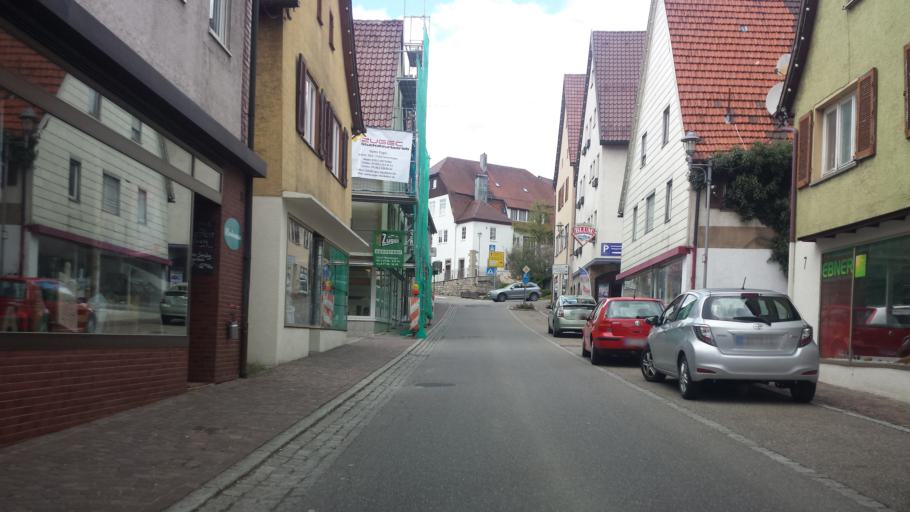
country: DE
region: Baden-Wuerttemberg
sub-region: Regierungsbezirk Stuttgart
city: Weissach
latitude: 48.8471
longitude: 8.9260
